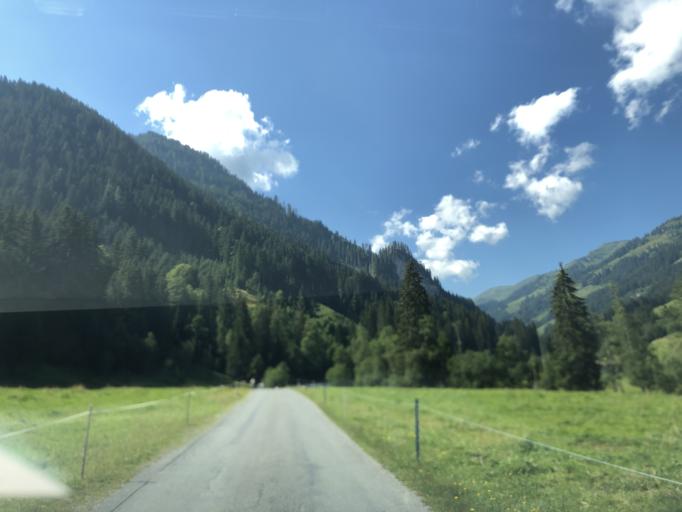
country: AT
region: Tyrol
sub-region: Politischer Bezirk Kitzbuhel
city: Kirchberg in Tirol
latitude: 47.3765
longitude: 12.3055
